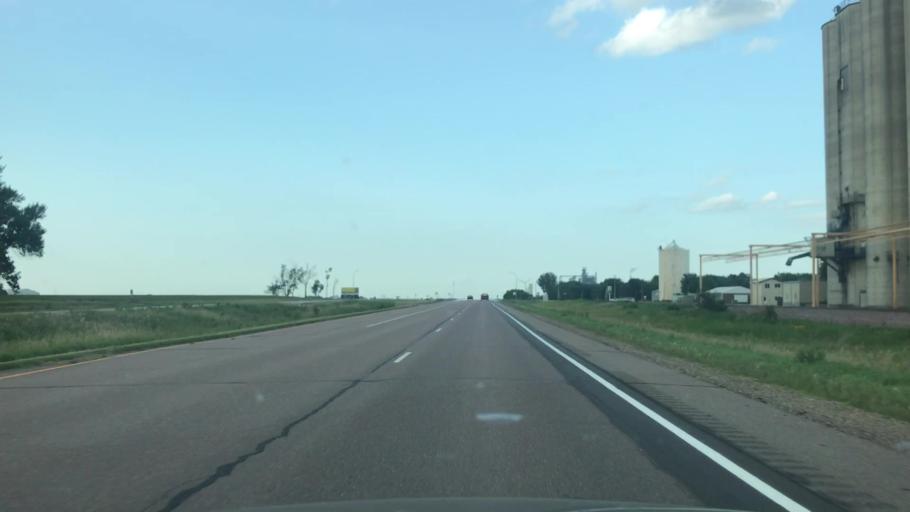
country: US
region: Minnesota
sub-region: Nobles County
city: Worthington
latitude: 43.6973
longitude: -95.4735
